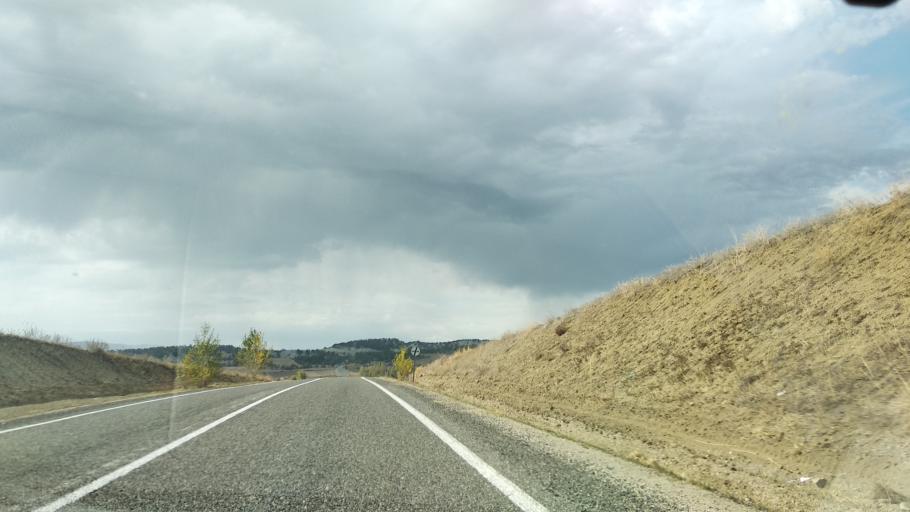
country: TR
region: Bolu
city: Seben
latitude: 40.3673
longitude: 31.5014
